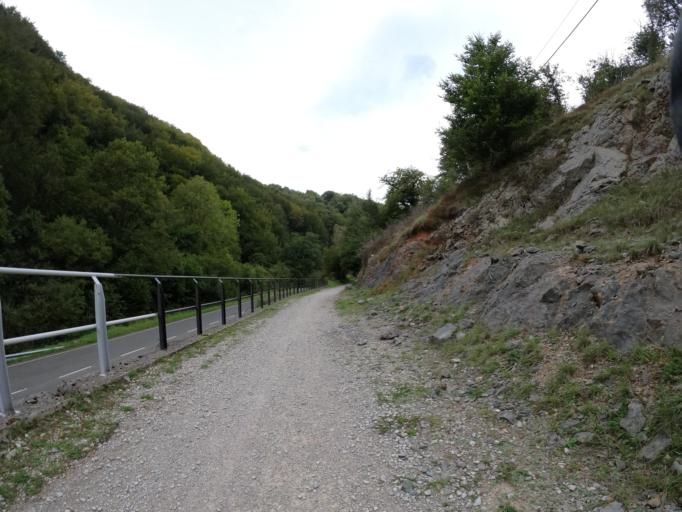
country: ES
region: Navarre
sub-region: Provincia de Navarra
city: Lekunberri
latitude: 43.0229
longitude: -1.9074
